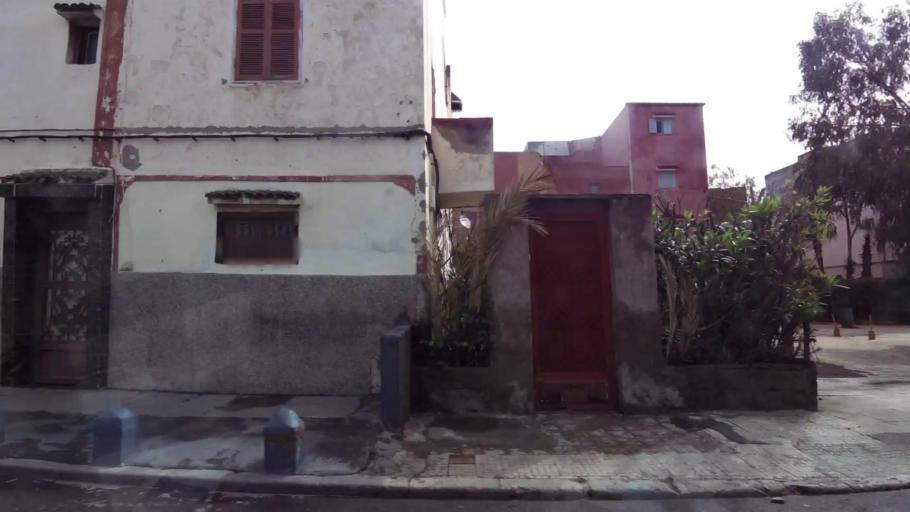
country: MA
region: Grand Casablanca
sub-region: Casablanca
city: Casablanca
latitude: 33.5732
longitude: -7.6714
